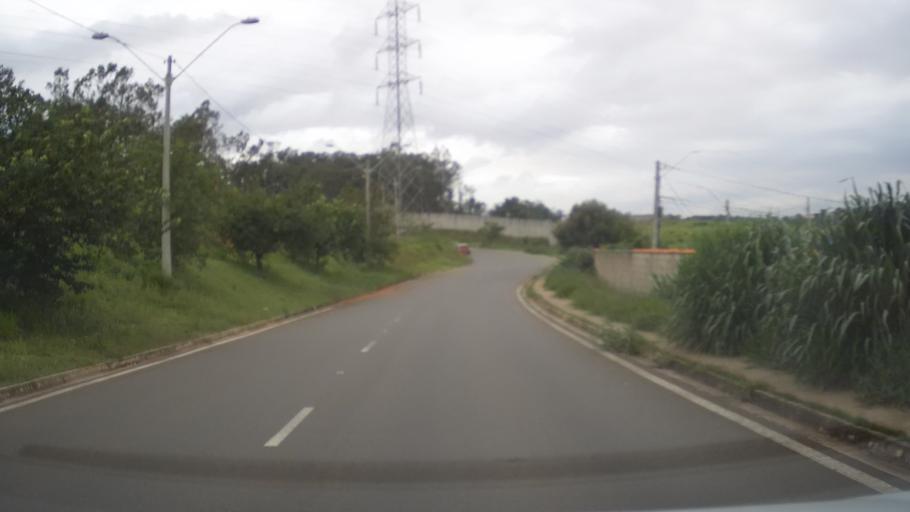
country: BR
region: Sao Paulo
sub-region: Campinas
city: Campinas
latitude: -22.9138
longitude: -47.0282
